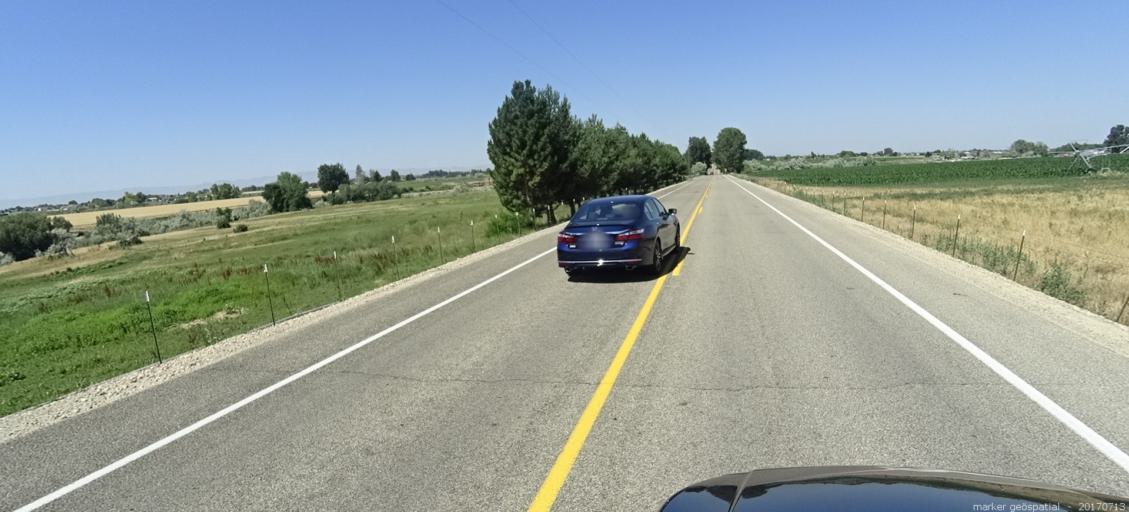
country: US
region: Idaho
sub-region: Ada County
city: Kuna
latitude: 43.5329
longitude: -116.4673
